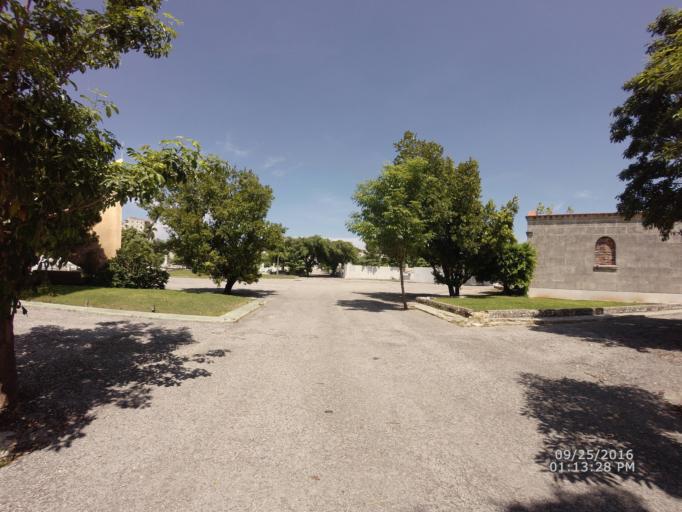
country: CU
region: La Habana
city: Havana
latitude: 23.1246
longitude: -82.4005
